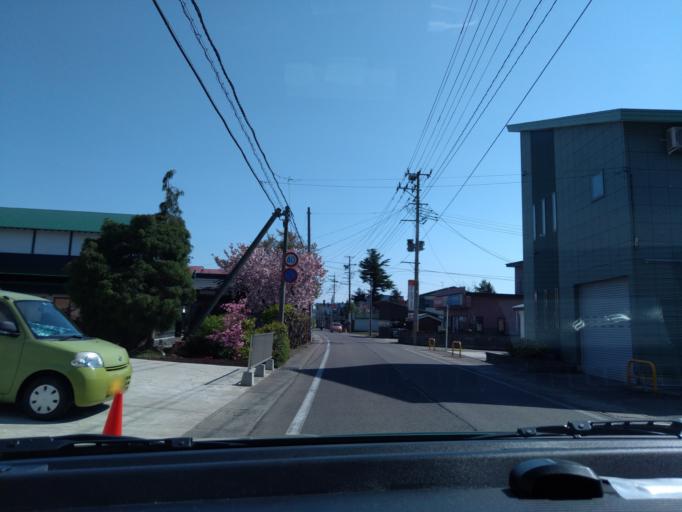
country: JP
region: Akita
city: Kakunodatemachi
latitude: 39.5024
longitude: 140.5946
